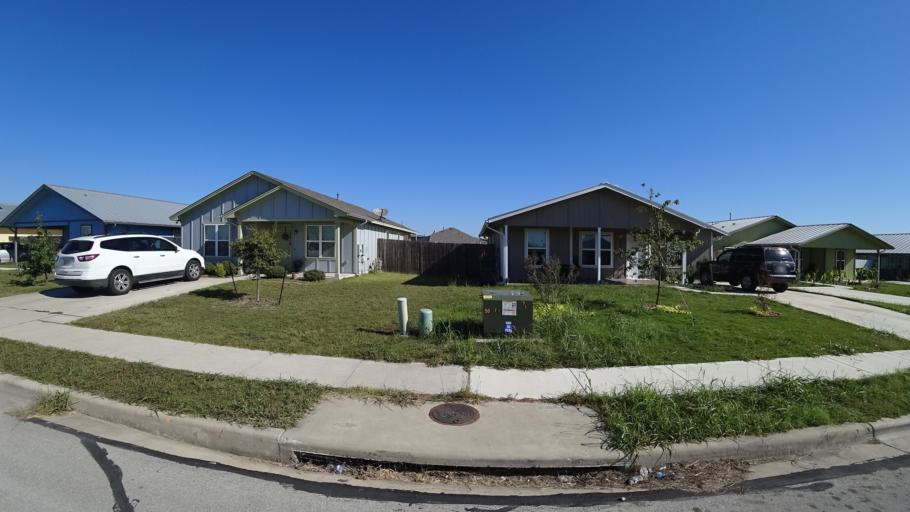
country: US
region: Texas
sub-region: Travis County
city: Hornsby Bend
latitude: 30.2572
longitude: -97.5896
